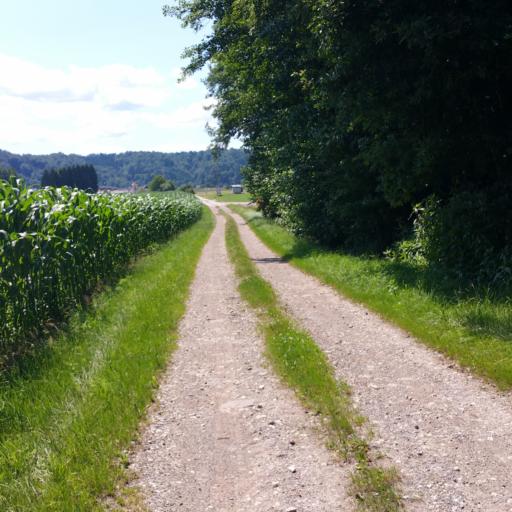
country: AT
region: Styria
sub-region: Politischer Bezirk Leibnitz
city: Gleinstatten
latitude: 46.7500
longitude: 15.3420
